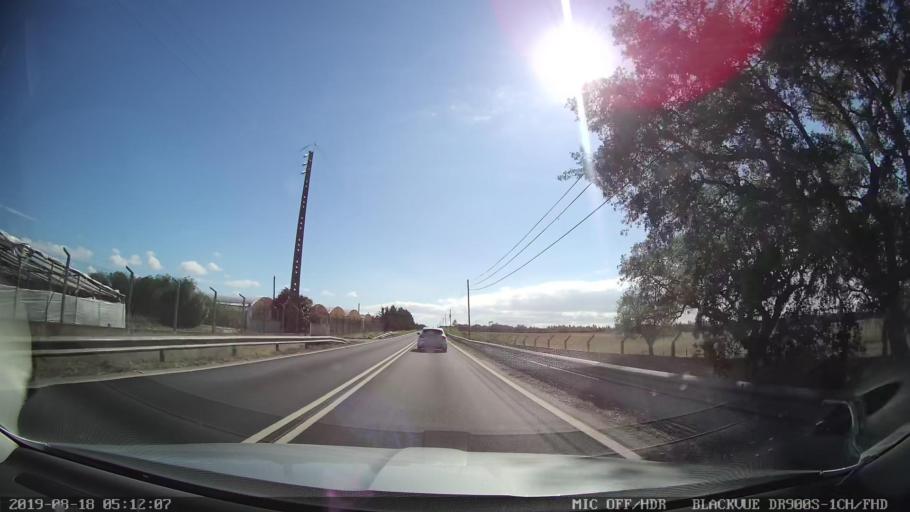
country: PT
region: Setubal
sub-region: Alcochete
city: Alcochete
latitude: 38.7713
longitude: -8.8942
